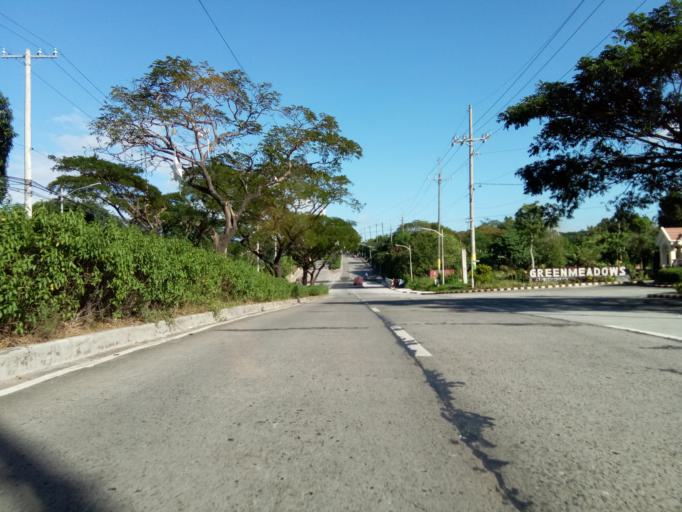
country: PH
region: Calabarzon
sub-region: Province of Cavite
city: Dasmarinas
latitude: 14.3503
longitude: 120.9641
